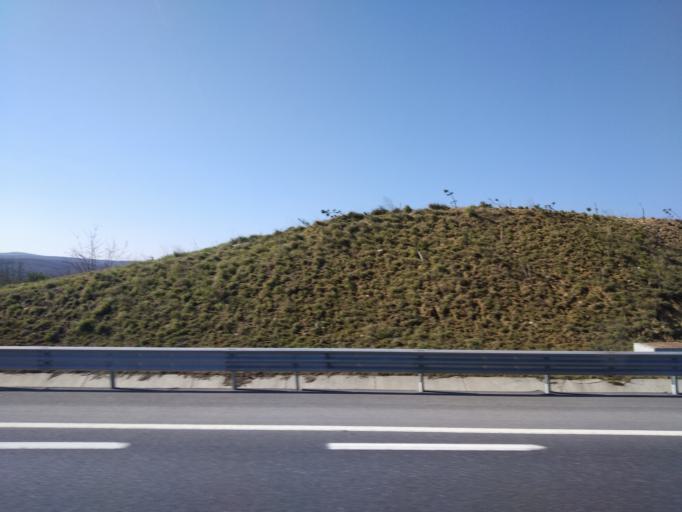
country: TR
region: Istanbul
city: Mahmut Sevket Pasa
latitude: 41.1301
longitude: 29.2862
